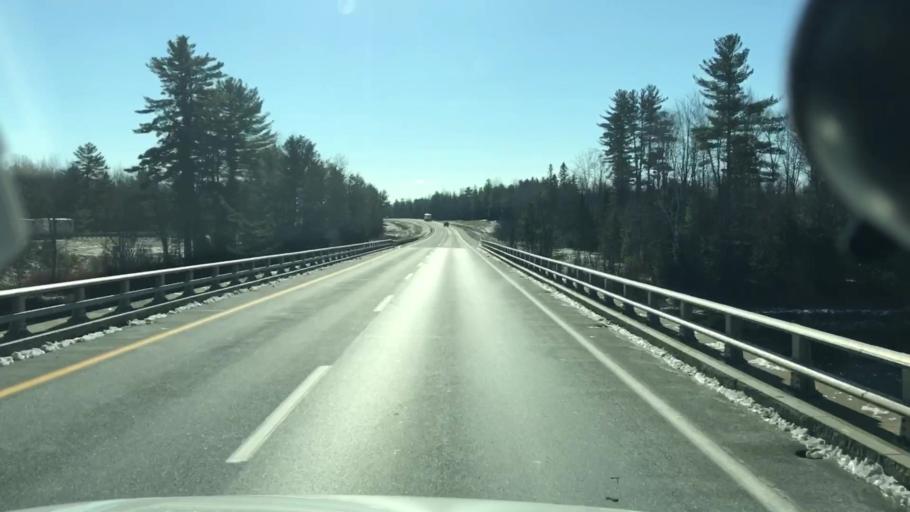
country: US
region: Maine
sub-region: Penobscot County
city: Howland
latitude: 45.2656
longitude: -68.6804
